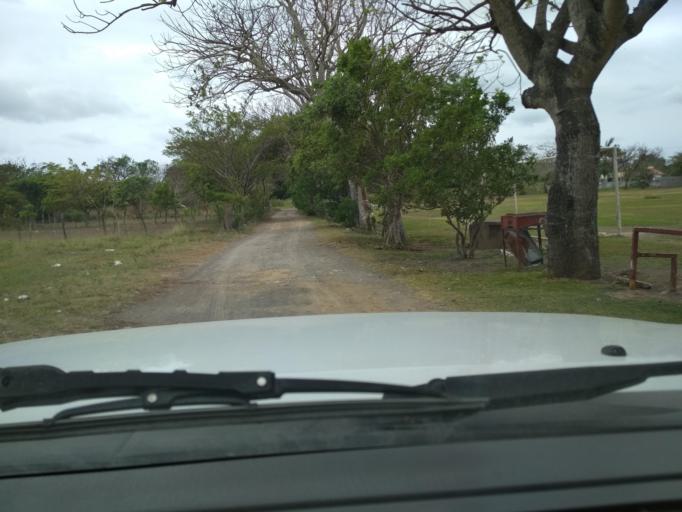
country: MX
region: Veracruz
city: Paso del Toro
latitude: 19.0490
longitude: -96.1344
